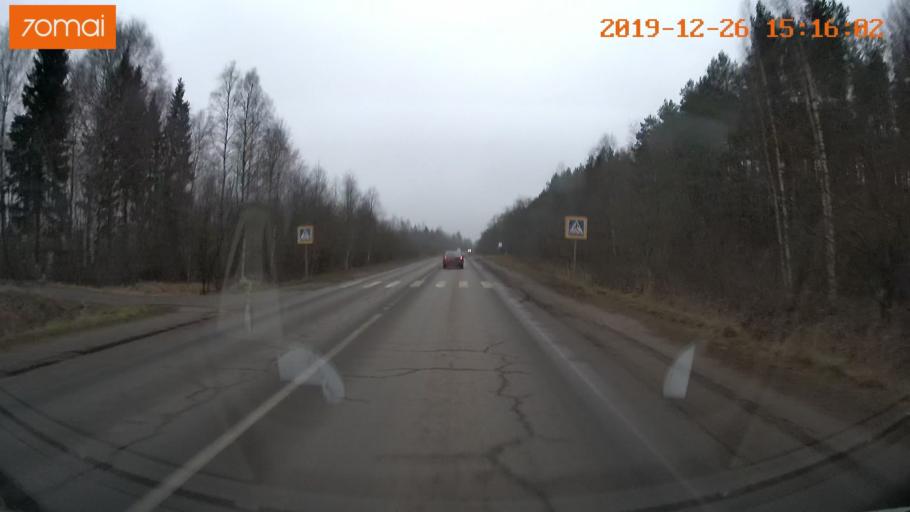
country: RU
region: Jaroslavl
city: Rybinsk
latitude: 58.0907
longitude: 38.8712
